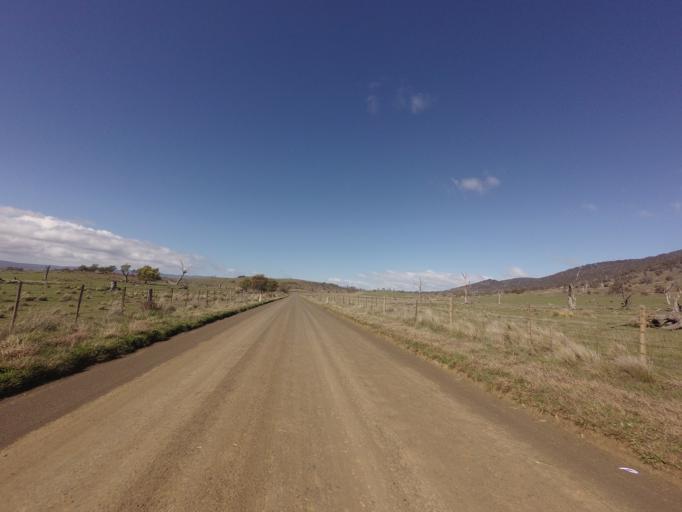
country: AU
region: Tasmania
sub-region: Northern Midlands
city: Evandale
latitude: -41.9266
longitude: 147.4106
